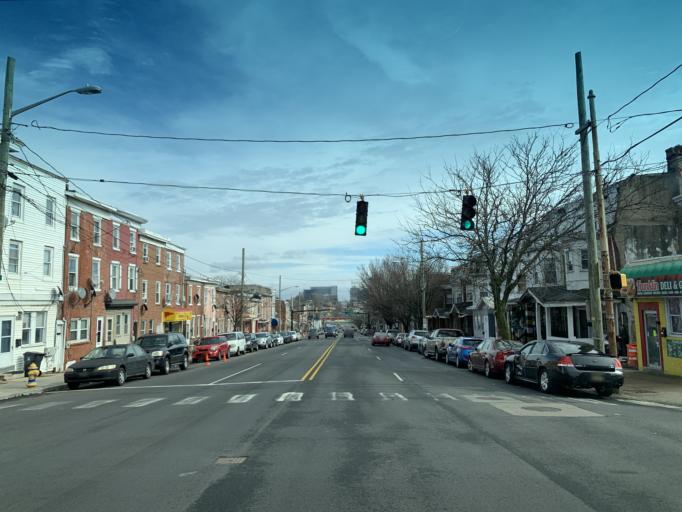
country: US
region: Delaware
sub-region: New Castle County
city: Wilmington
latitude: 39.7456
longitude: -75.5642
